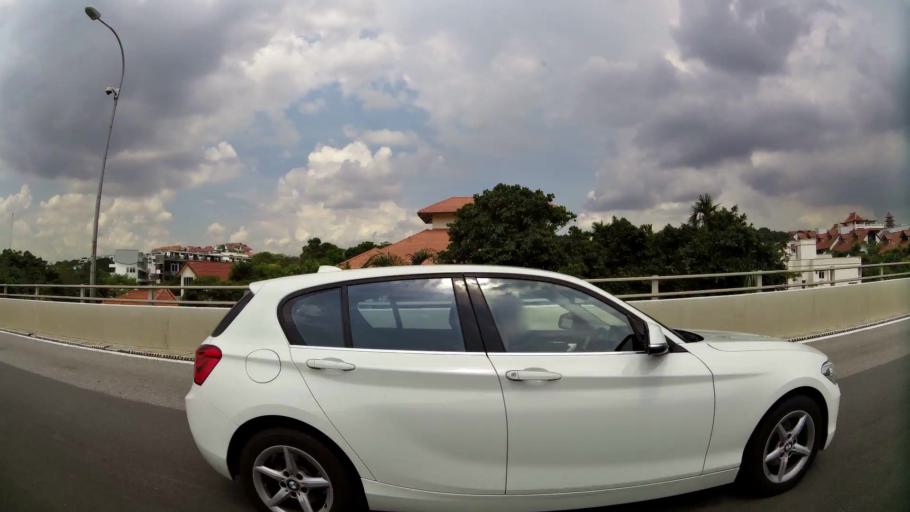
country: SG
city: Singapore
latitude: 1.2782
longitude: 103.7866
